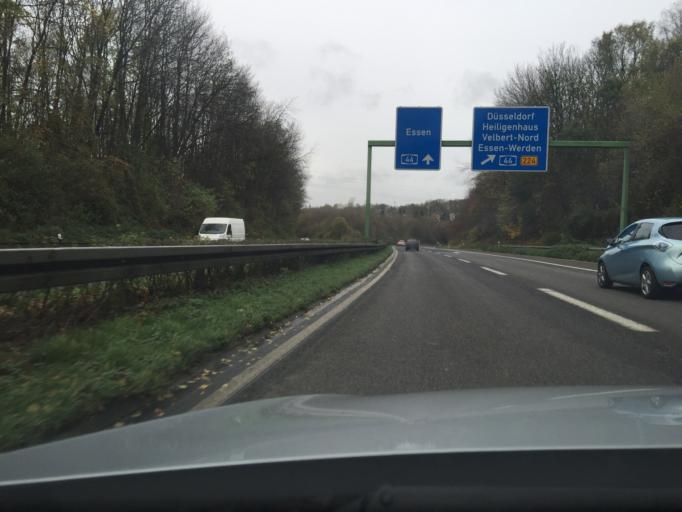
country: DE
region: North Rhine-Westphalia
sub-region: Regierungsbezirk Dusseldorf
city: Velbert
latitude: 51.3494
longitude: 7.0441
